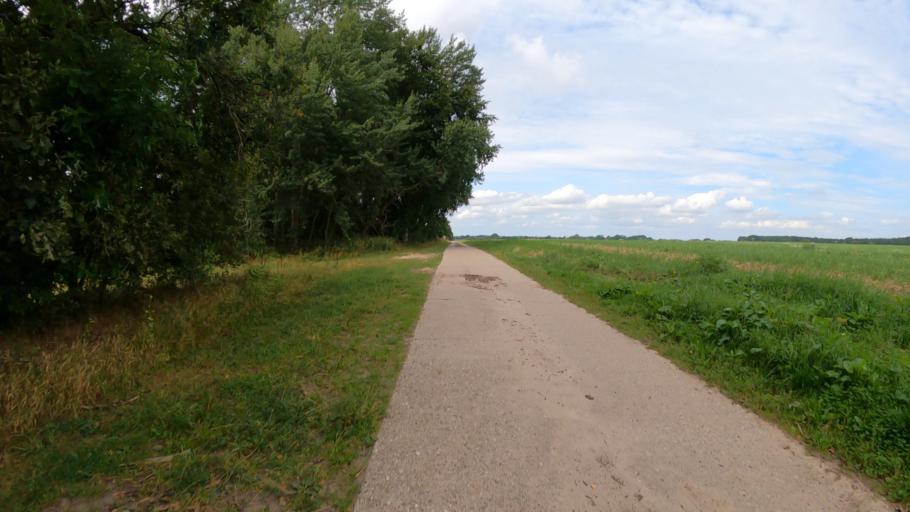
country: DE
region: Lower Saxony
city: Neu Wulmstorf
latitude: 53.4292
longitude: 9.8241
